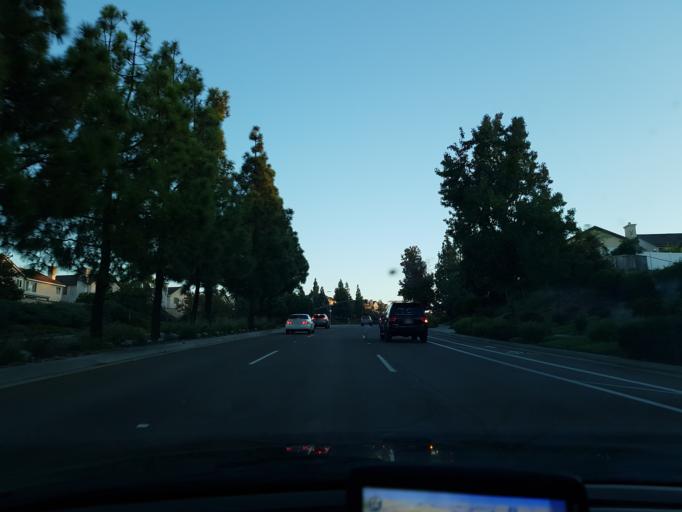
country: US
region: California
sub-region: San Diego County
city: Fairbanks Ranch
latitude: 32.9261
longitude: -117.1248
